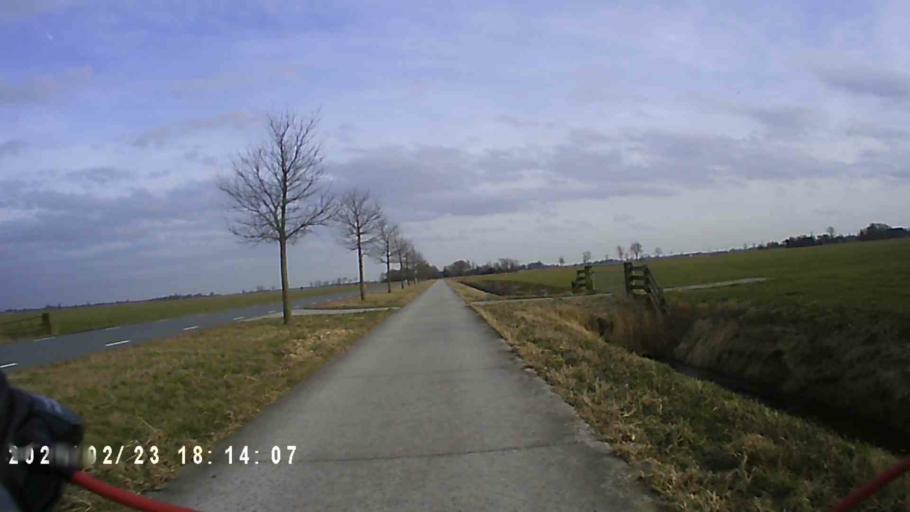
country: NL
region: Groningen
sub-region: Gemeente Bedum
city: Bedum
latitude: 53.3871
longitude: 6.6240
